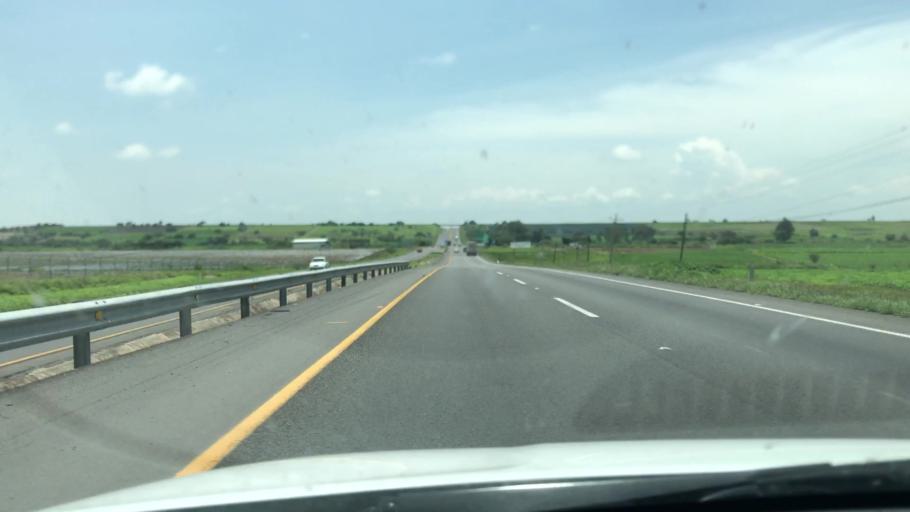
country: MX
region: Guanajuato
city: Penjamo
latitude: 20.3823
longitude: -101.8092
